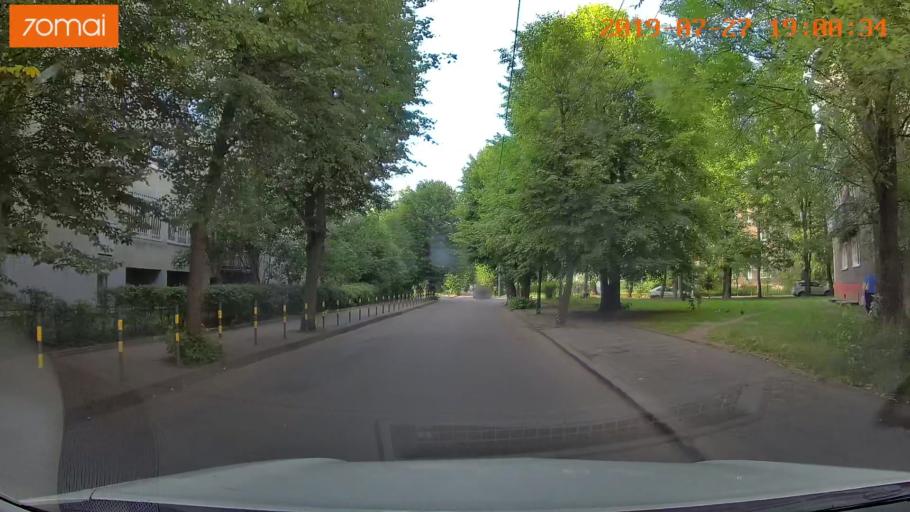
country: RU
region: Kaliningrad
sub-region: Gorod Kaliningrad
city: Kaliningrad
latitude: 54.7272
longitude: 20.4846
